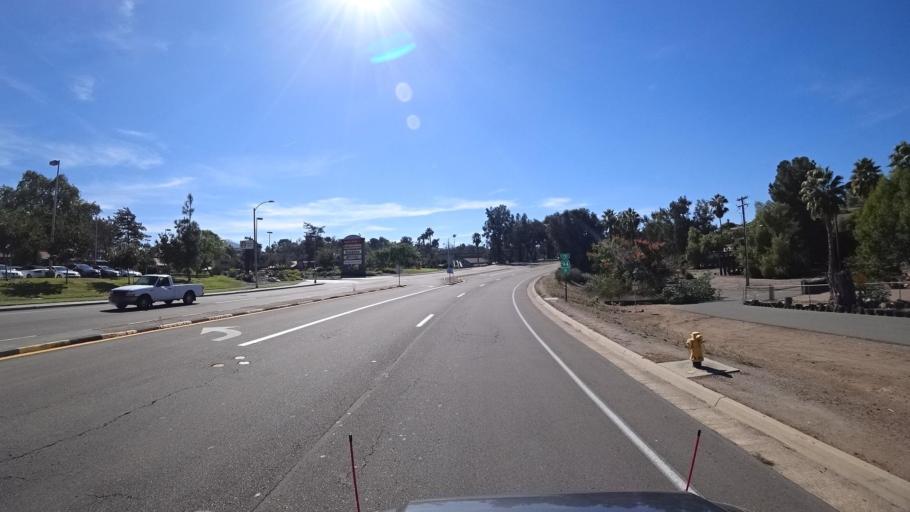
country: US
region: California
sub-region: San Diego County
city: Casa de Oro-Mount Helix
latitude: 32.7478
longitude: -116.9622
